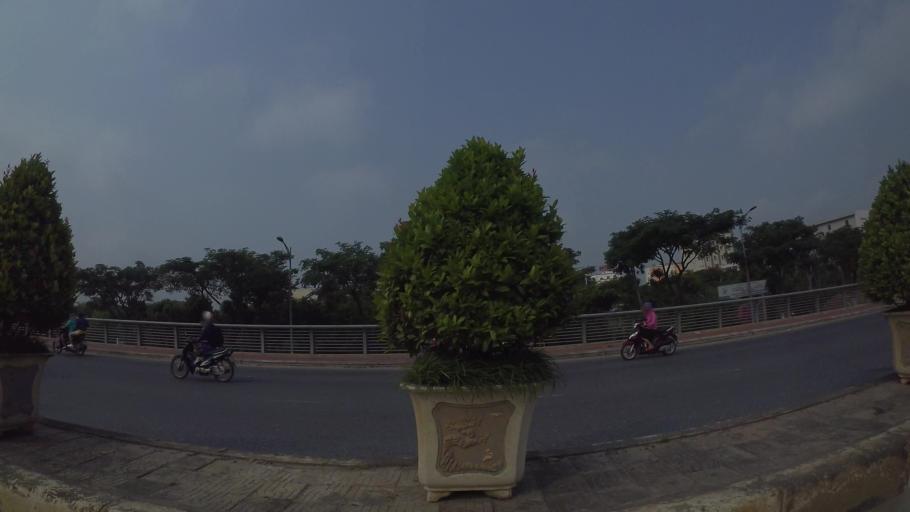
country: VN
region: Da Nang
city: Cam Le
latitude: 16.0192
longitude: 108.2116
